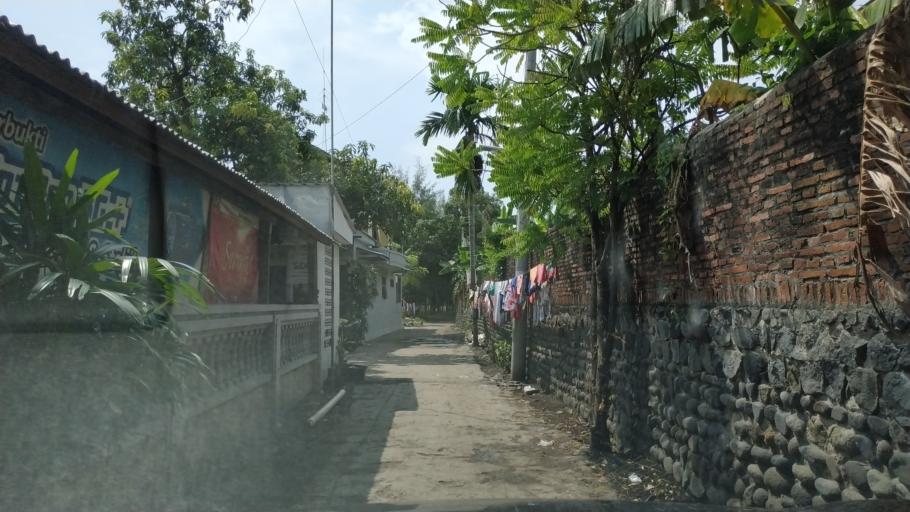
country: ID
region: Central Java
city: Tegal
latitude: -6.8633
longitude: 109.1767
